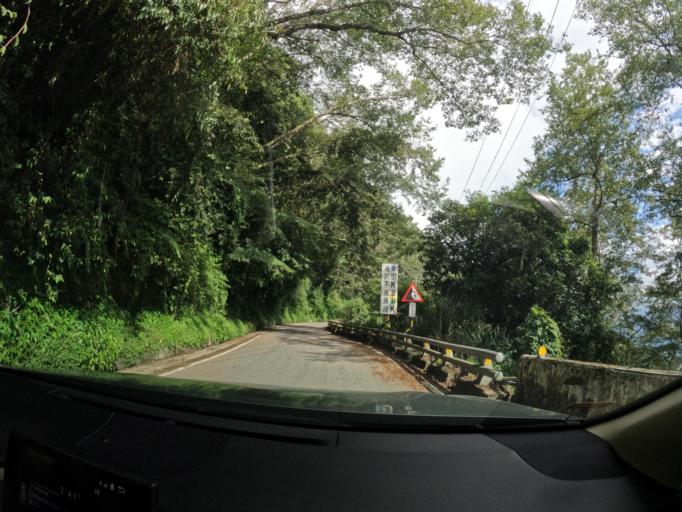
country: TW
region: Taiwan
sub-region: Taitung
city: Taitung
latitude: 23.2239
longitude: 121.0097
